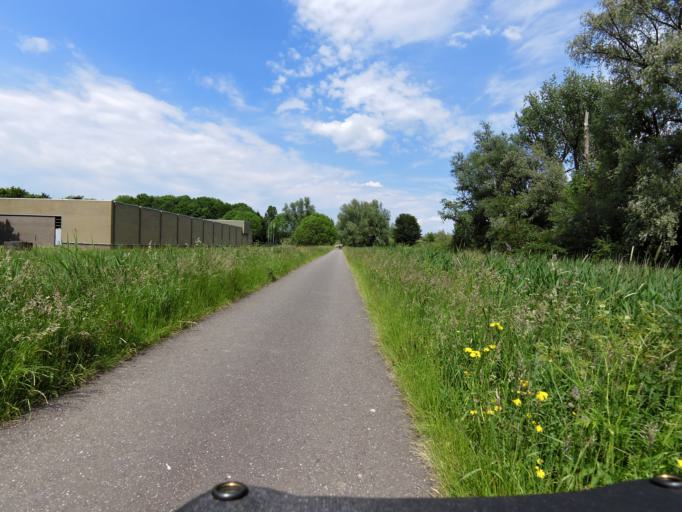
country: NL
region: North Brabant
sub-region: Gemeente Woudrichem
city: Woudrichem
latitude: 51.8099
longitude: 5.0607
